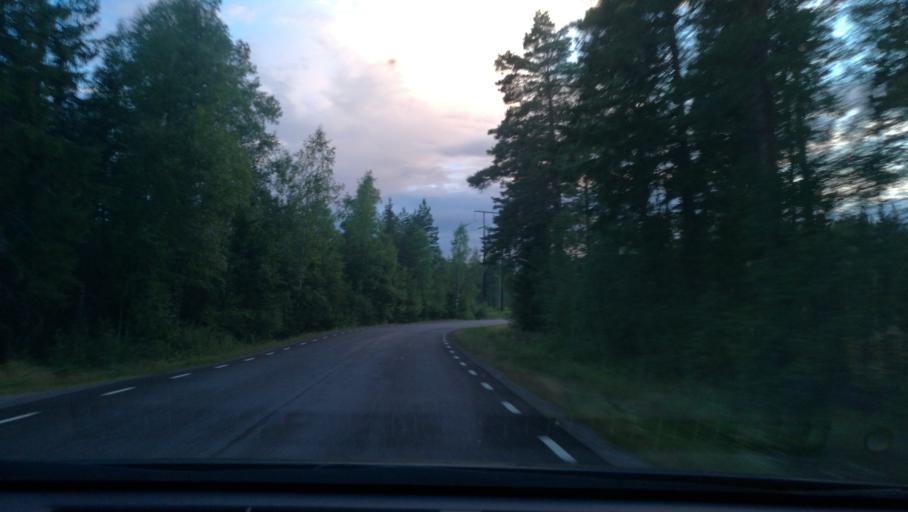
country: SE
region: OEstergoetland
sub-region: Norrkopings Kommun
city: Svartinge
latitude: 58.8194
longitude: 16.0454
